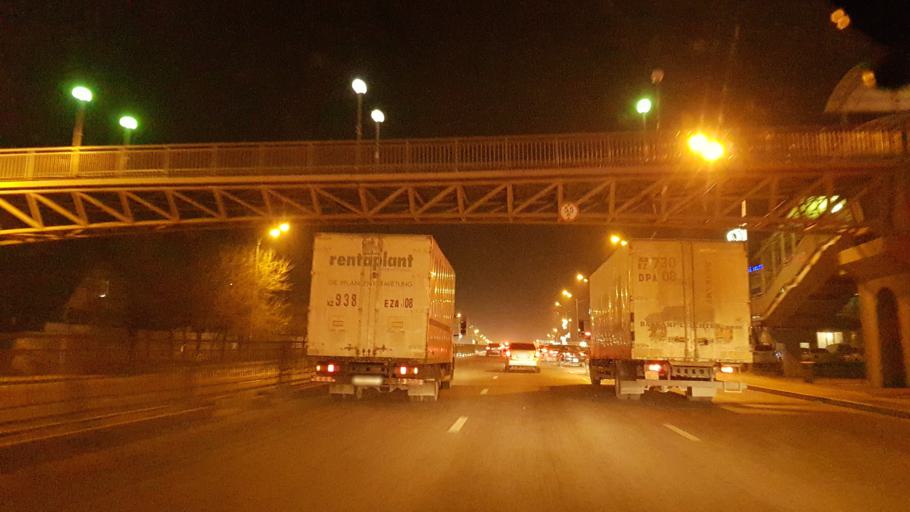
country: KZ
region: Almaty Qalasy
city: Almaty
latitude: 43.2670
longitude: 76.8711
